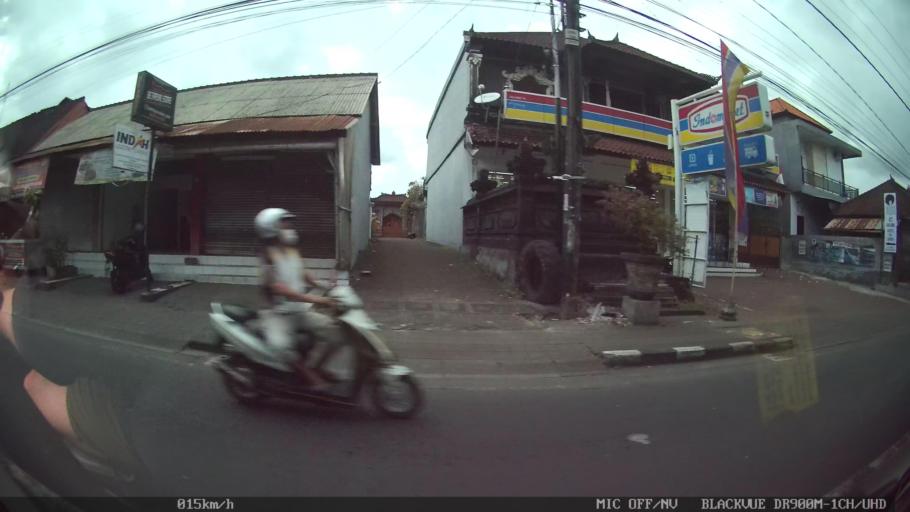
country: ID
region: Bali
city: Banjar Karangsuling
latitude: -8.6090
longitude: 115.1724
